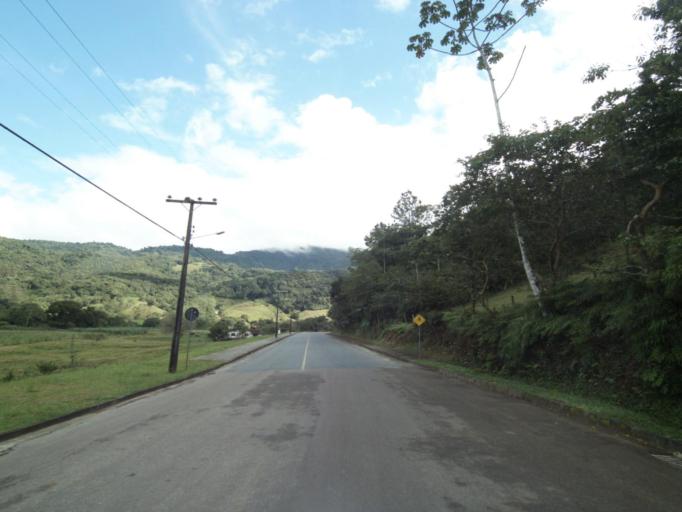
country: BR
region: Santa Catarina
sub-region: Pomerode
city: Pomerode
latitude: -26.6783
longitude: -49.1807
